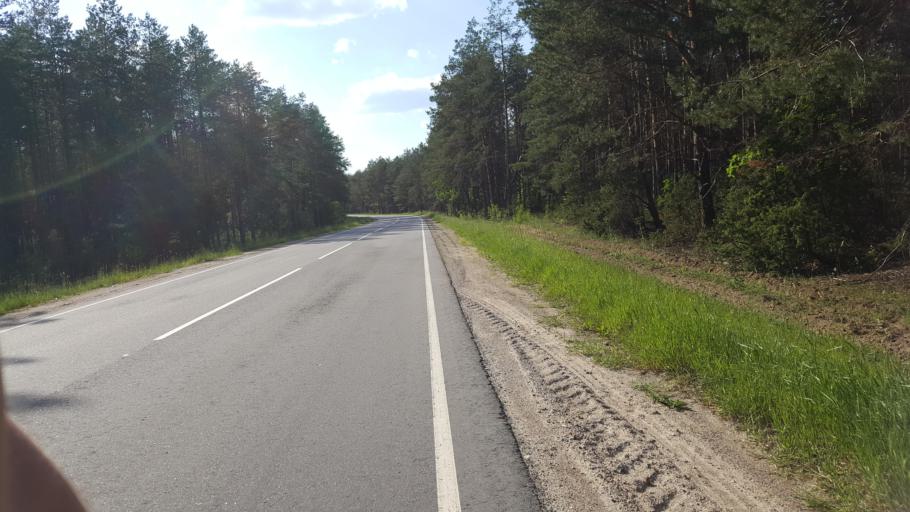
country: BY
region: Brest
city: Zhabinka
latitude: 52.3980
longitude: 24.0880
